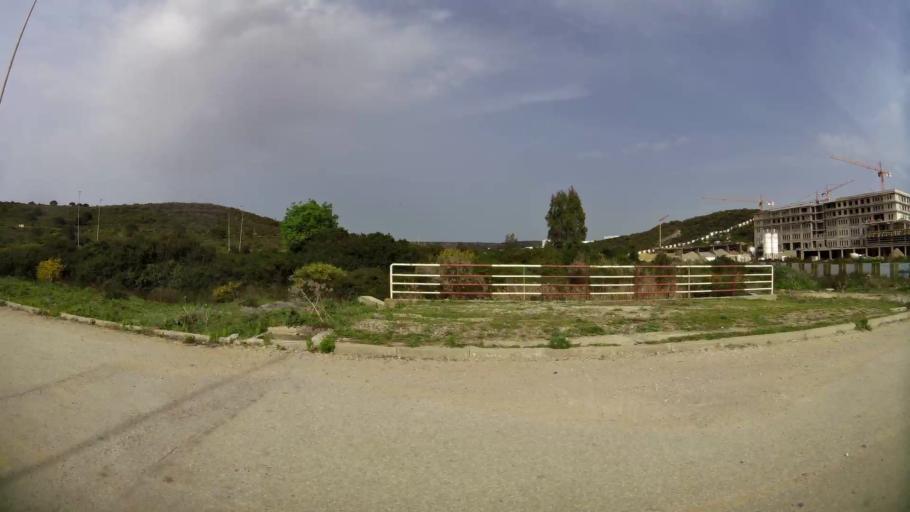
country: MA
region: Tanger-Tetouan
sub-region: Tanger-Assilah
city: Boukhalef
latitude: 35.6857
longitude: -5.9291
